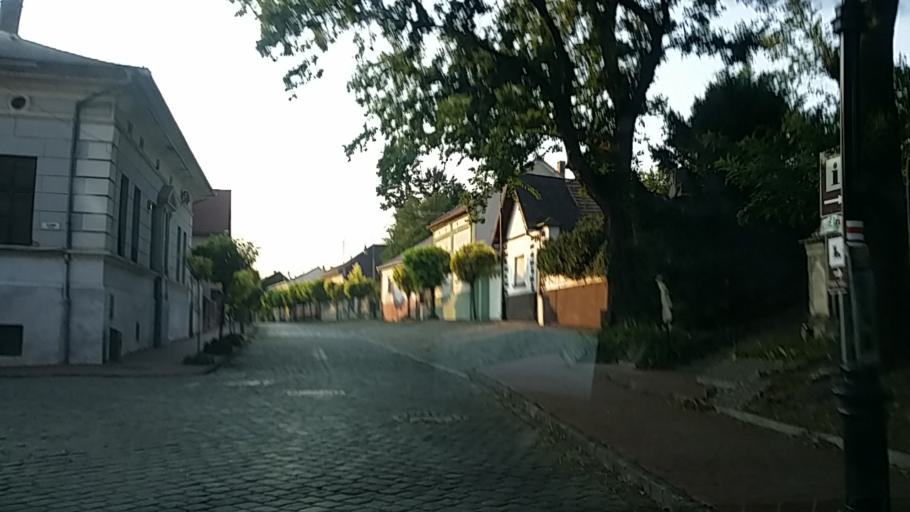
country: HU
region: Tolna
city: Dunafoldvar
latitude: 46.8092
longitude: 18.9262
